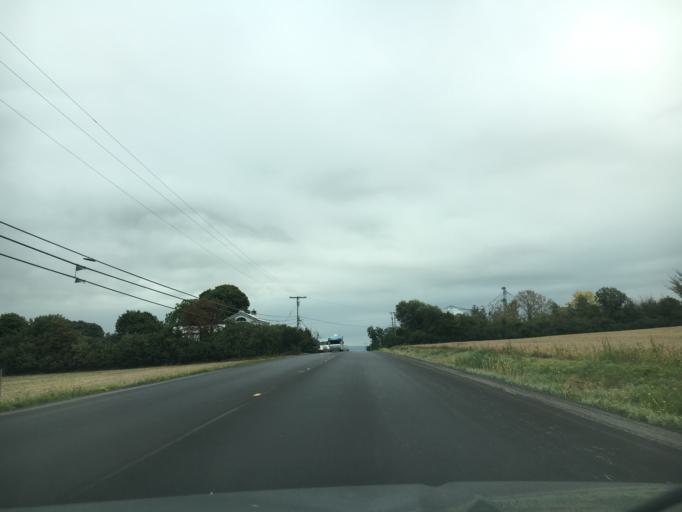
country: US
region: New York
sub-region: Cayuga County
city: Union Springs
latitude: 42.6809
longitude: -76.8150
